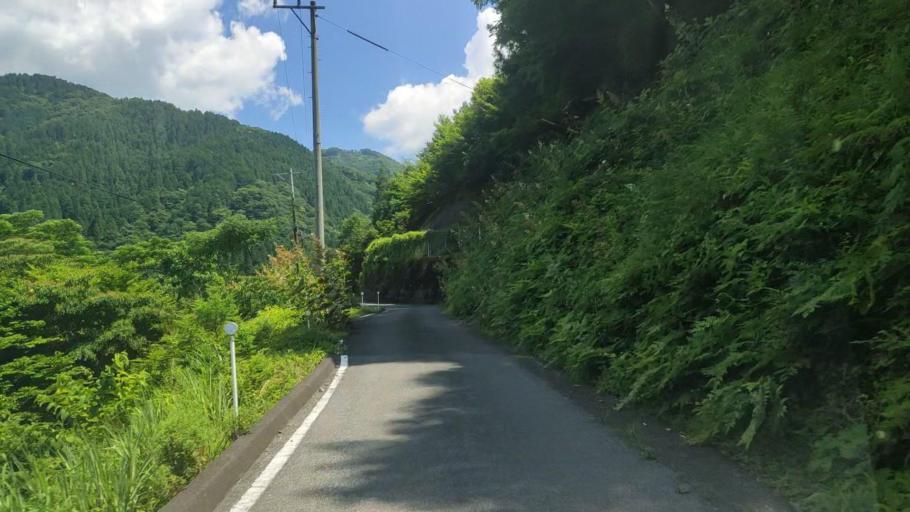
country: JP
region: Fukui
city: Ono
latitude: 35.7211
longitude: 136.5819
